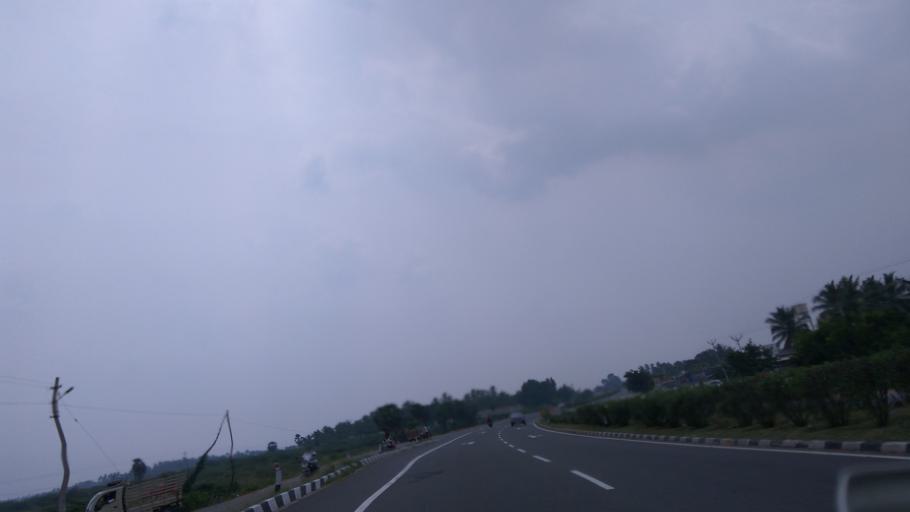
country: IN
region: Tamil Nadu
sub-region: Dharmapuri
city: Dharmapuri
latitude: 12.2193
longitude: 78.1916
